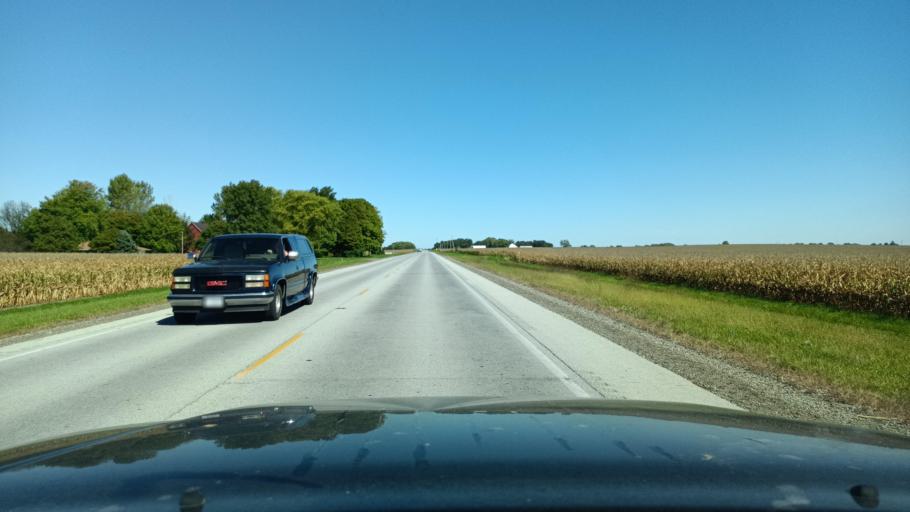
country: US
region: Illinois
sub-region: Champaign County
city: Philo
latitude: 40.0622
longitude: -88.1618
